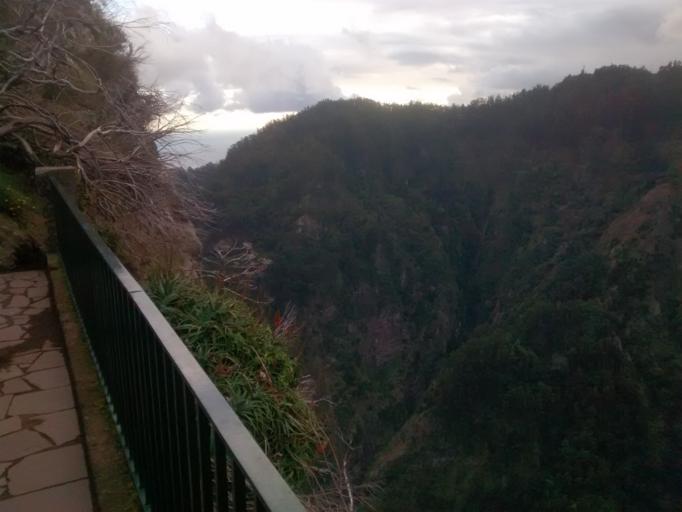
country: PT
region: Madeira
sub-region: Camara de Lobos
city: Curral das Freiras
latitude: 32.7102
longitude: -16.9658
